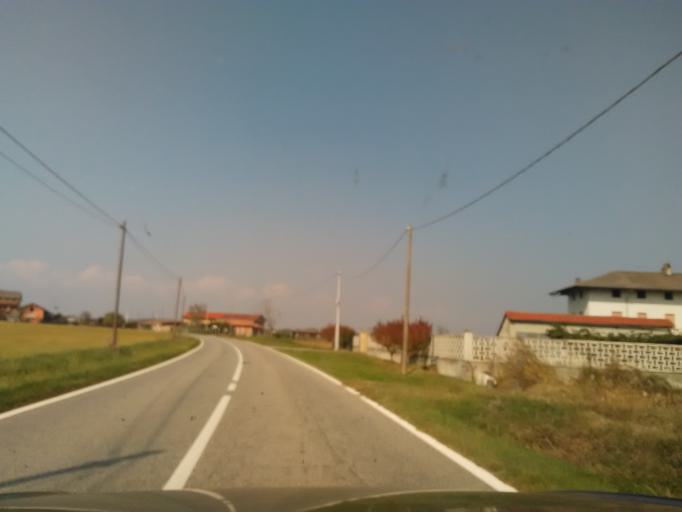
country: IT
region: Piedmont
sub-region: Provincia di Vercelli
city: Santhia
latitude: 45.3782
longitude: 8.1709
